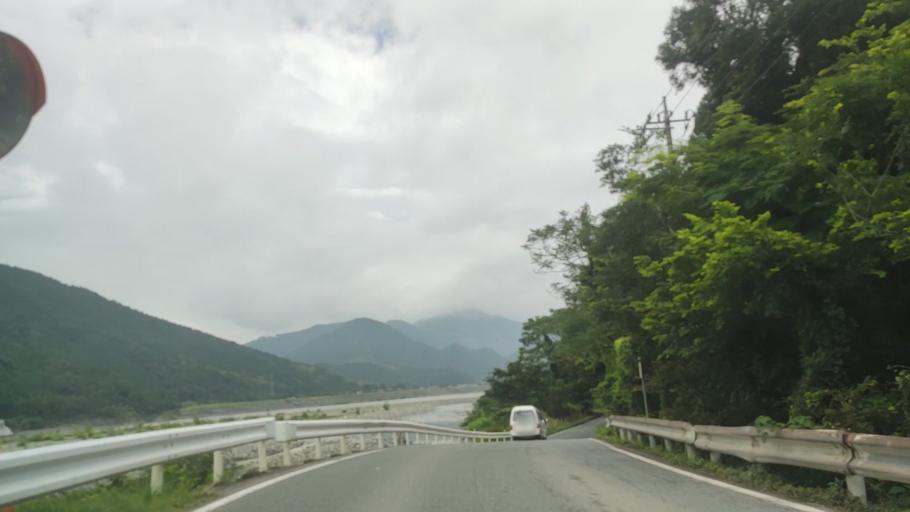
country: JP
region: Shizuoka
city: Fujinomiya
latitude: 35.2123
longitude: 138.5448
